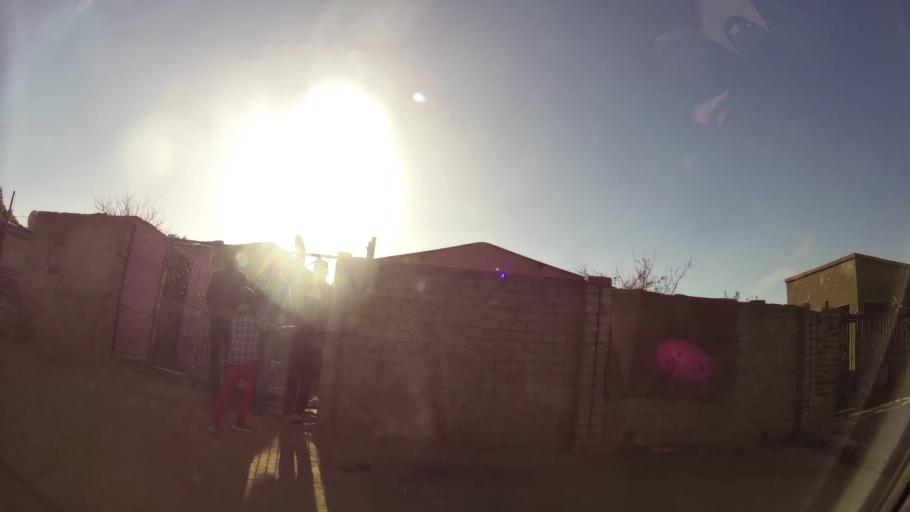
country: ZA
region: Gauteng
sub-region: City of Johannesburg Metropolitan Municipality
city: Diepsloot
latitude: -25.9263
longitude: 28.0042
